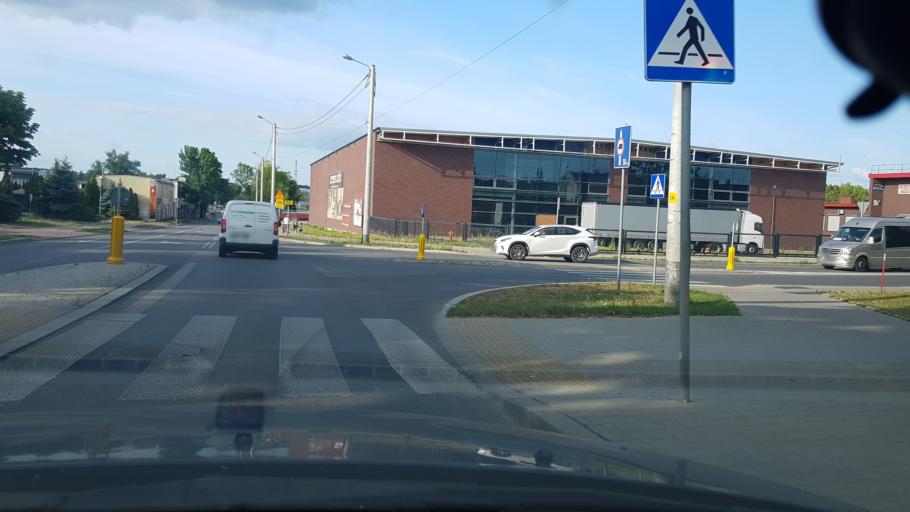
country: PL
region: Lodz Voivodeship
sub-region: Powiat tomaszowski
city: Tomaszow Mazowiecki
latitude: 51.5476
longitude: 20.0150
